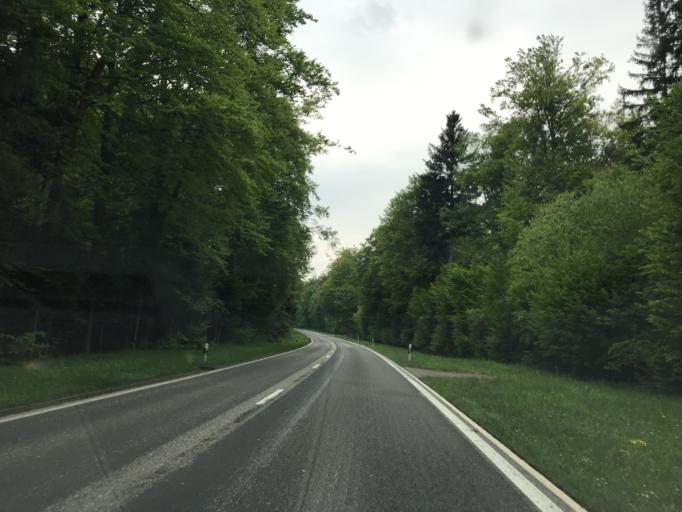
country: CH
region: Bern
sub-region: Oberaargau
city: Aarwangen
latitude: 47.2488
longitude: 7.7492
